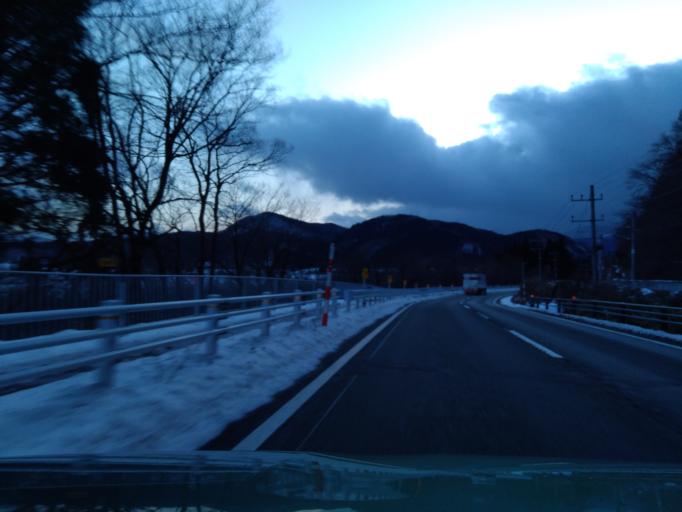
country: JP
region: Iwate
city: Shizukuishi
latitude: 39.6898
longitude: 140.9232
